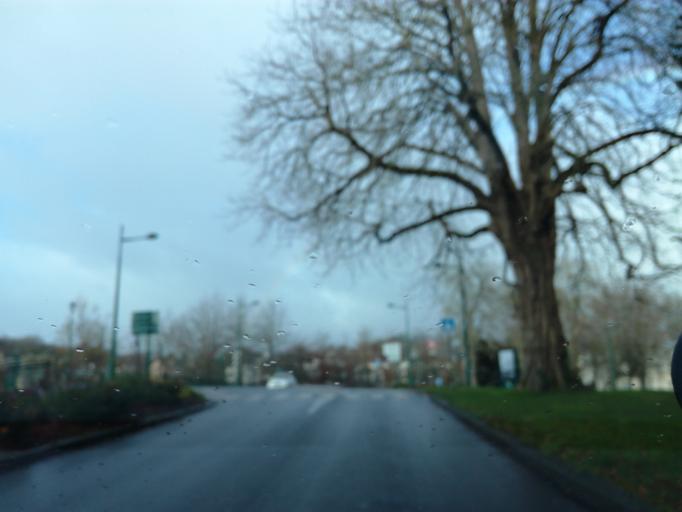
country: FR
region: Brittany
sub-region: Departement du Morbihan
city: Pontivy
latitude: 48.0595
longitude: -2.9688
